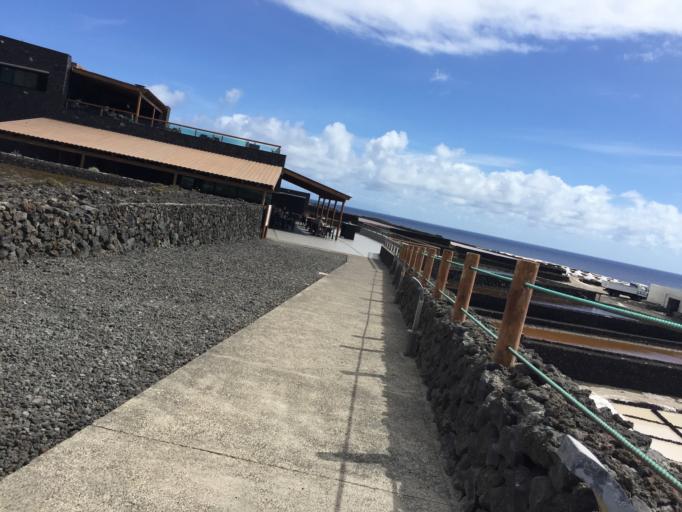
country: ES
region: Canary Islands
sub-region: Provincia de Santa Cruz de Tenerife
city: Fuencaliente de la Palma
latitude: 28.4546
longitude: -17.8425
